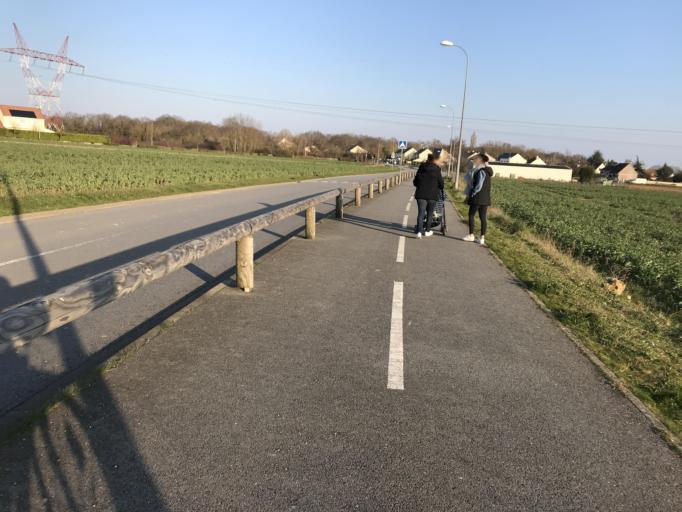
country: FR
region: Ile-de-France
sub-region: Departement de l'Essonne
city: Villejust
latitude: 48.6794
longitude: 2.2368
